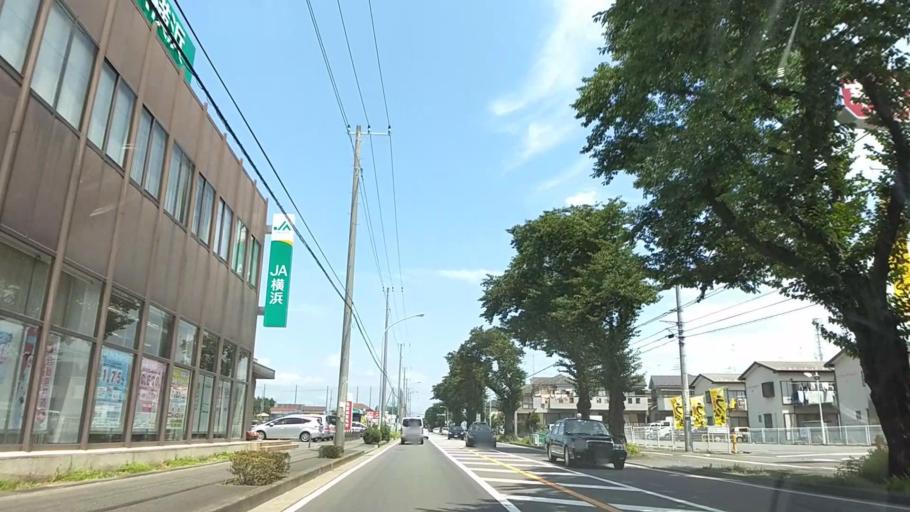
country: JP
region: Kanagawa
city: Minami-rinkan
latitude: 35.4784
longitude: 139.4805
